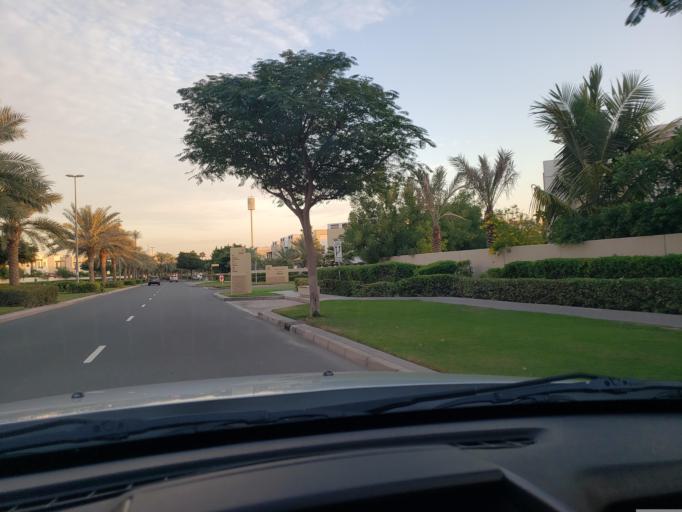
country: AE
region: Dubai
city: Dubai
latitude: 25.0229
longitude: 55.2724
